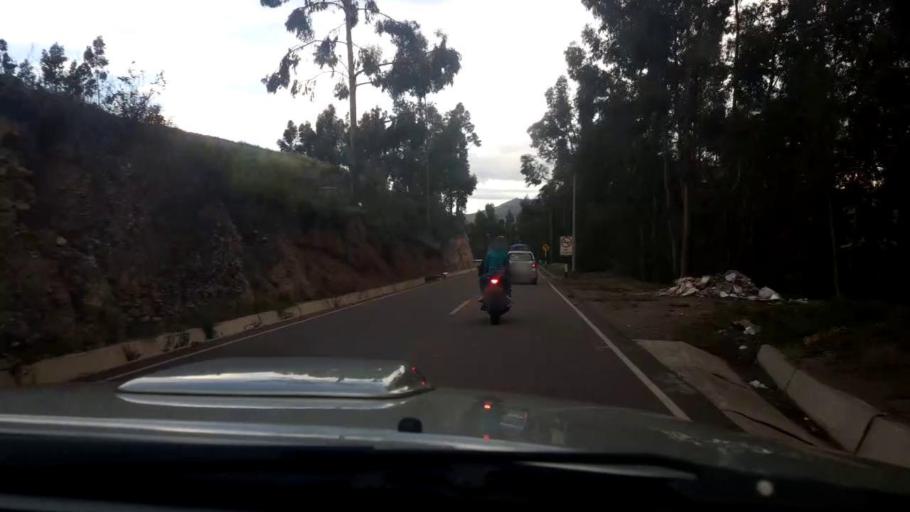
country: PE
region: Ayacucho
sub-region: Provincia de Huamanga
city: Carmen Alto
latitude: -13.2283
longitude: -74.2292
